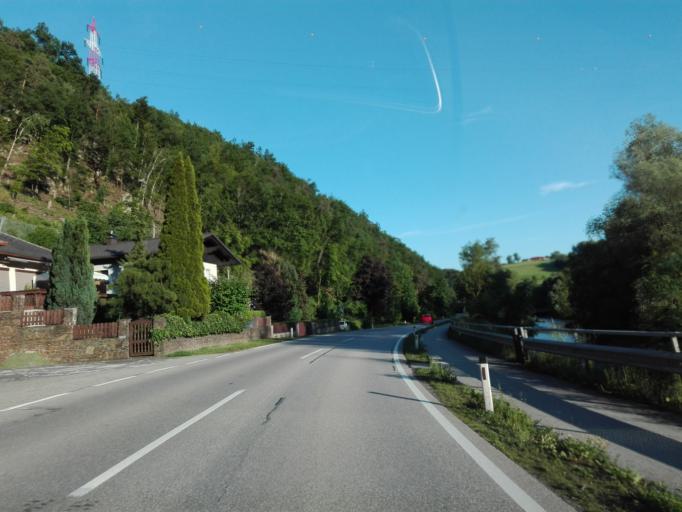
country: AT
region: Upper Austria
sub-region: Politischer Bezirk Rohrbach
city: Kleinzell im Muehlkreis
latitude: 48.3768
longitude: 13.9569
